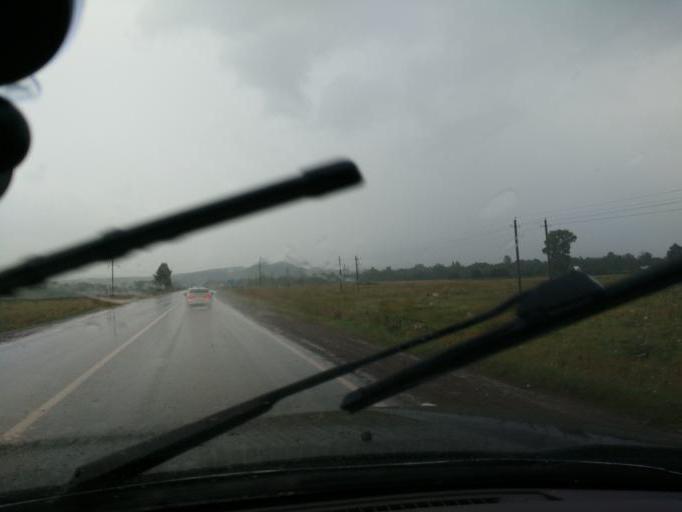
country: RU
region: Perm
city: Osa
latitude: 57.1803
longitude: 55.5538
